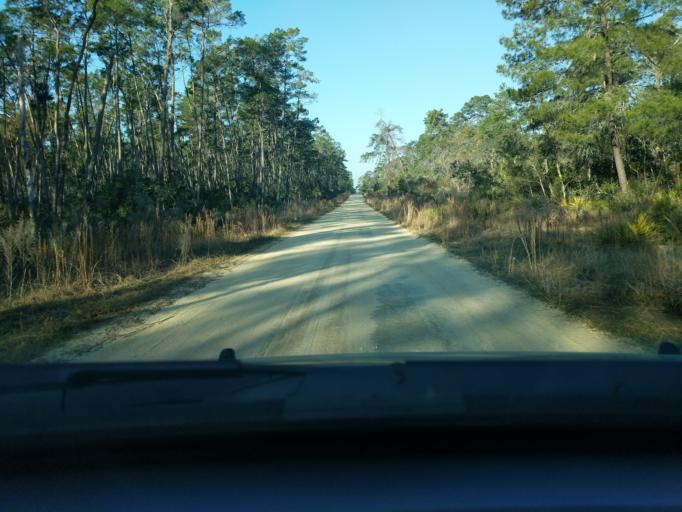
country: US
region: Florida
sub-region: Marion County
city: Silver Springs Shores
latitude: 29.2264
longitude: -81.8136
